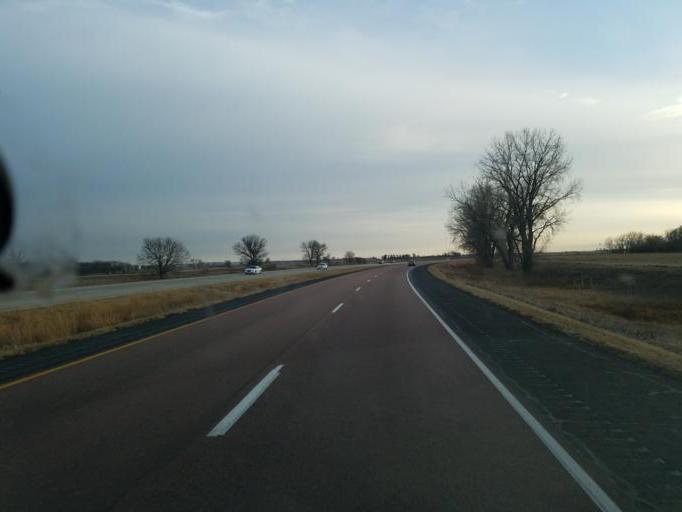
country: US
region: Iowa
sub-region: Monona County
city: Onawa
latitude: 41.9733
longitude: -96.1019
